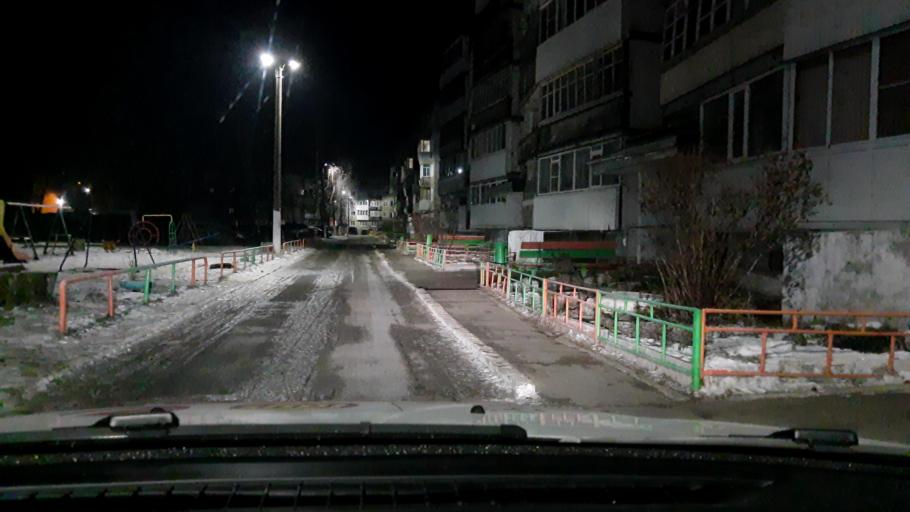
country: RU
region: Nizjnij Novgorod
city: Volodarsk
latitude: 56.2392
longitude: 43.1873
